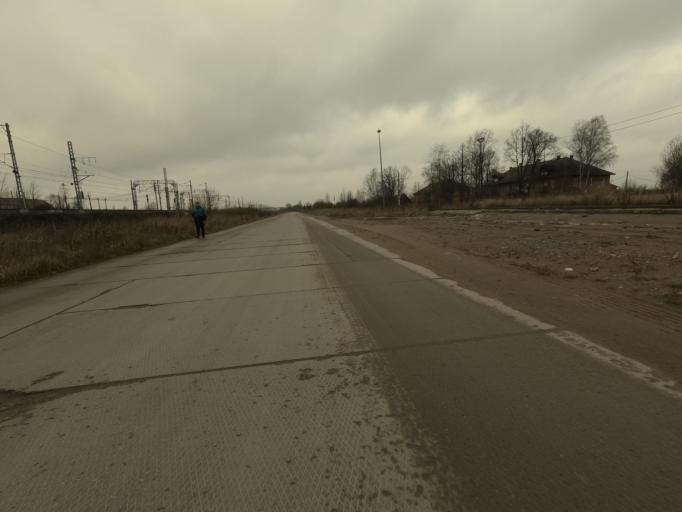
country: RU
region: Leningrad
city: Lyuban'
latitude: 59.4750
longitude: 31.2560
